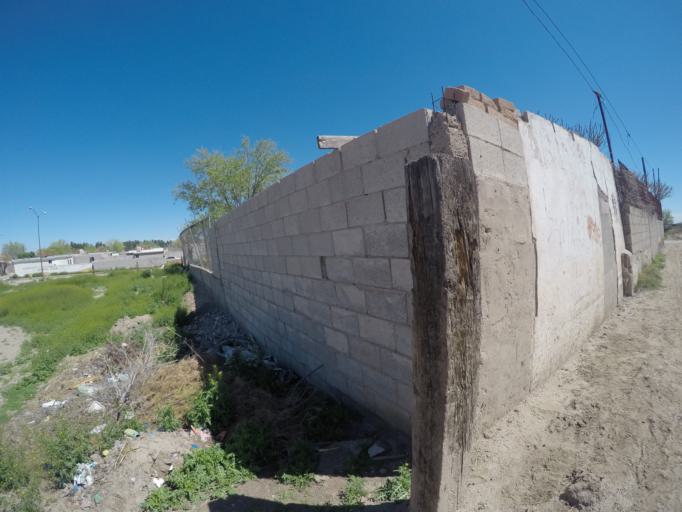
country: US
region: Texas
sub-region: El Paso County
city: Socorro Mission Number 1 Colonia
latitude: 31.6077
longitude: -106.3120
